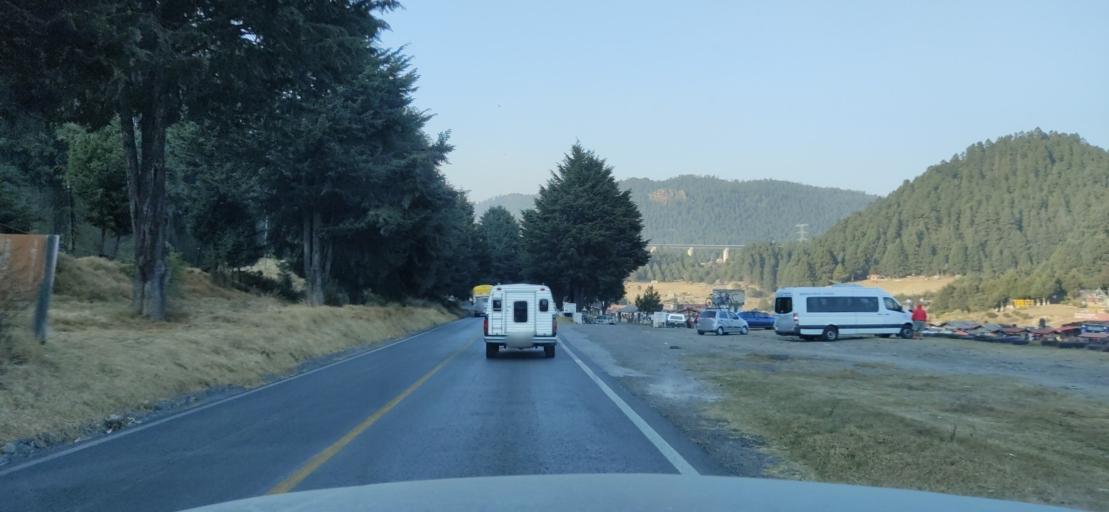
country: MX
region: Mexico
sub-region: Ocoyoacac
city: San Jeronimo Acazulco
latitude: 19.2856
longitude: -99.3743
